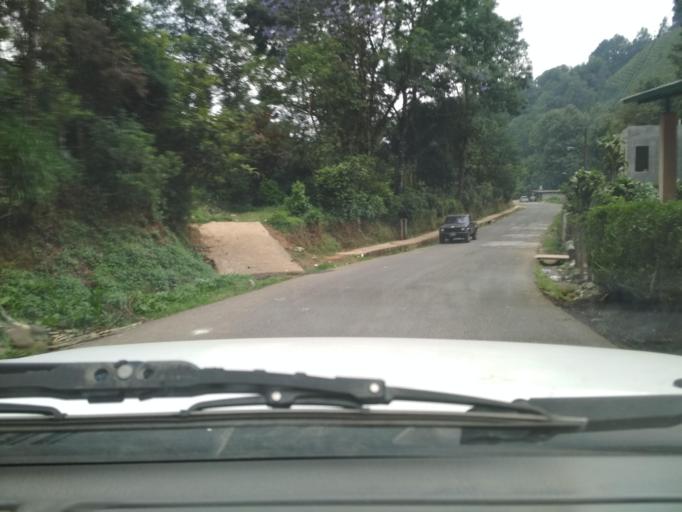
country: MX
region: Veracruz
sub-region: La Perla
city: Barrio de San Miguel
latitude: 18.9388
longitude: -97.1279
